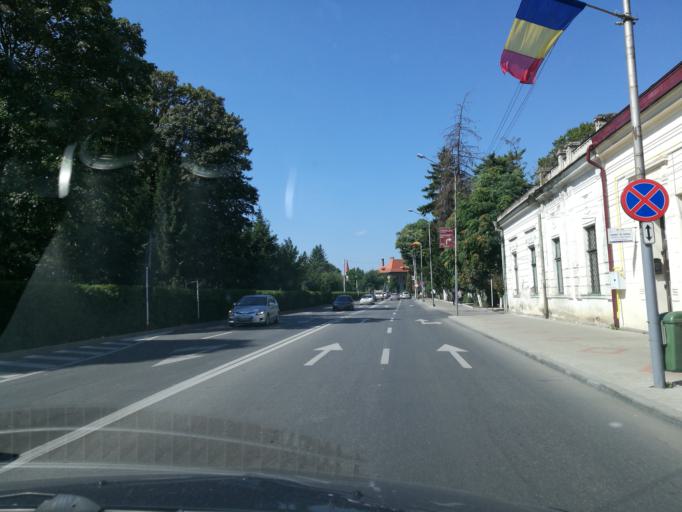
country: RO
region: Suceava
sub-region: Municipiul Suceava
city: Radauti
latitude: 47.8433
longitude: 25.9200
